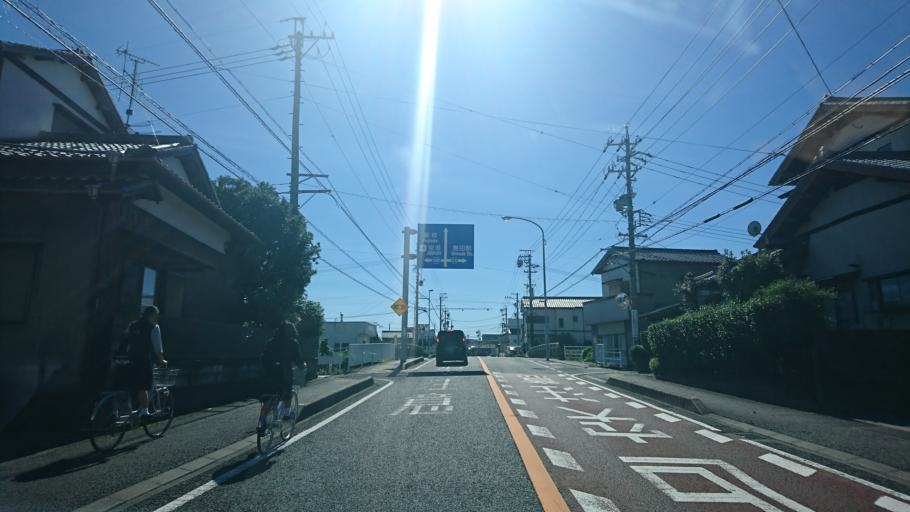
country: JP
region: Shizuoka
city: Shimada
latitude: 34.8397
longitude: 138.1798
